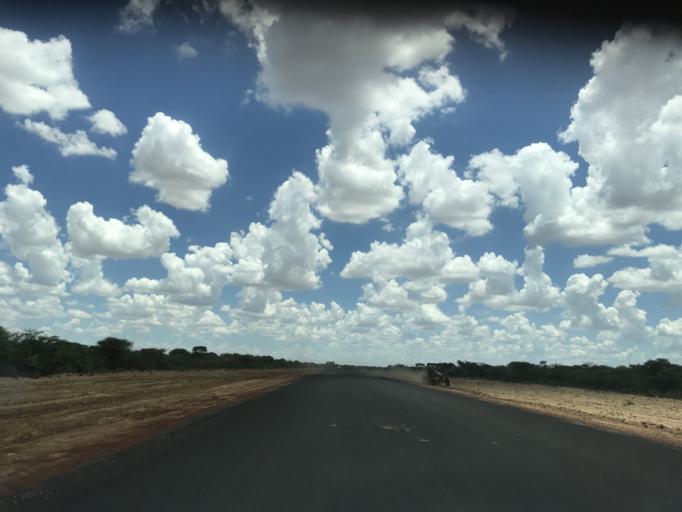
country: BW
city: Mabuli
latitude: -25.8056
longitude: 24.6828
